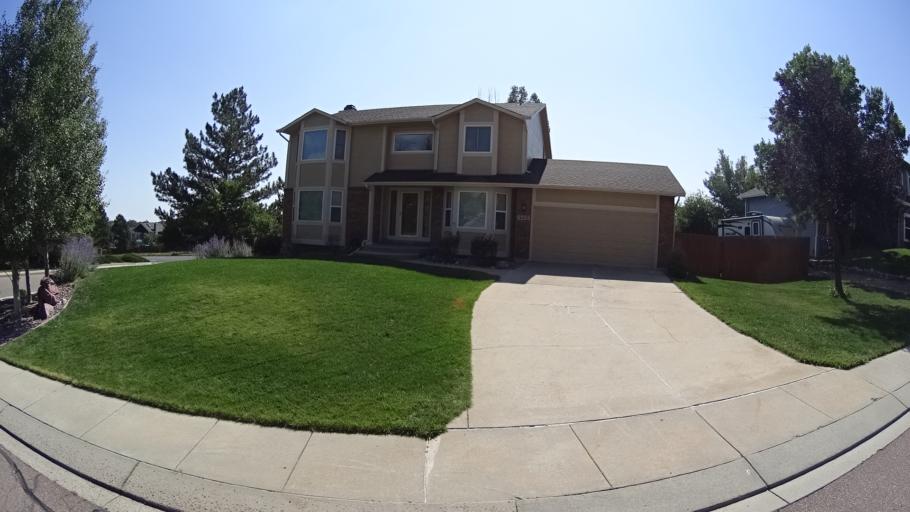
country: US
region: Colorado
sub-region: El Paso County
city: Air Force Academy
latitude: 38.9212
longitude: -104.8690
